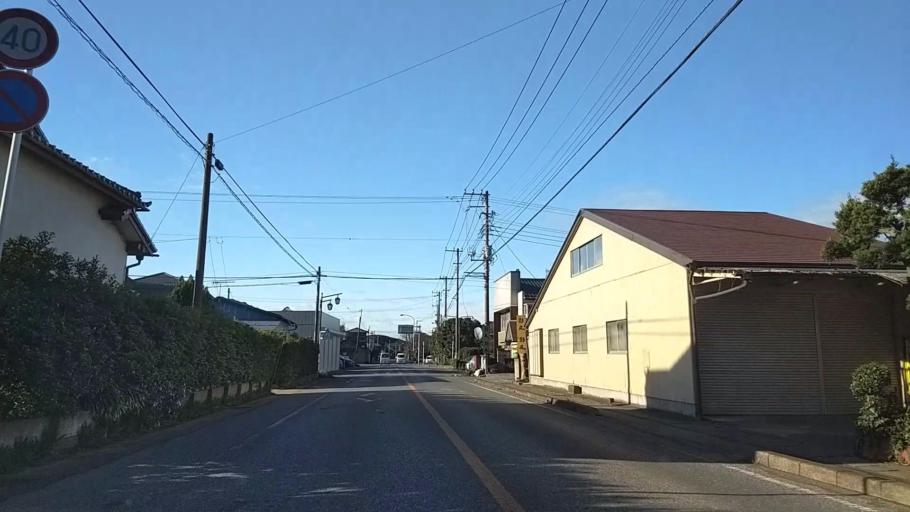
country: JP
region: Chiba
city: Futtsu
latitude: 35.3216
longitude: 139.8412
